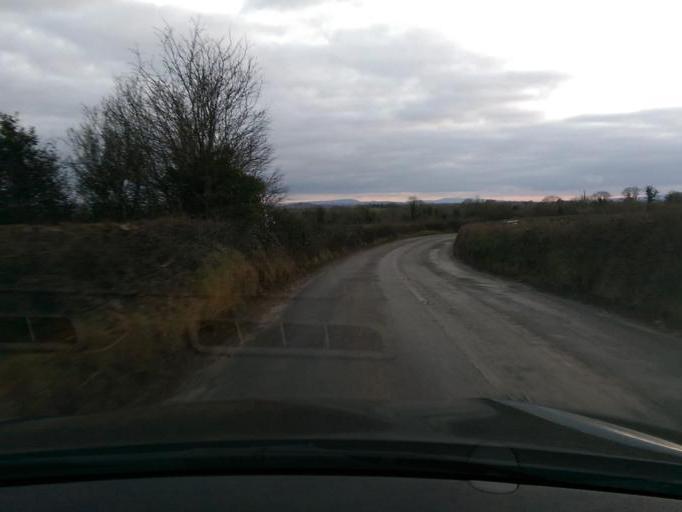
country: IE
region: Connaught
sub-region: County Galway
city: Portumna
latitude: 53.1108
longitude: -8.1147
